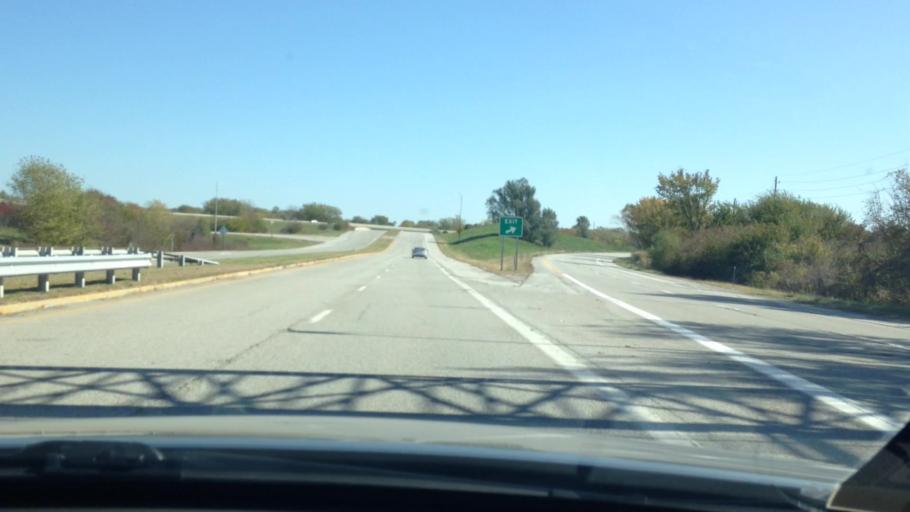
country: US
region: Missouri
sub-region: Platte County
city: Weatherby Lake
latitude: 39.3109
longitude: -94.6769
